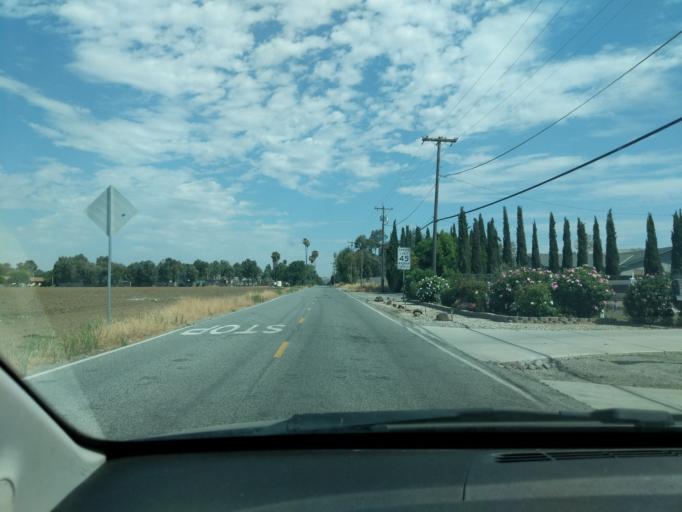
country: US
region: California
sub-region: Santa Clara County
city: San Martin
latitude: 37.0785
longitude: -121.5726
